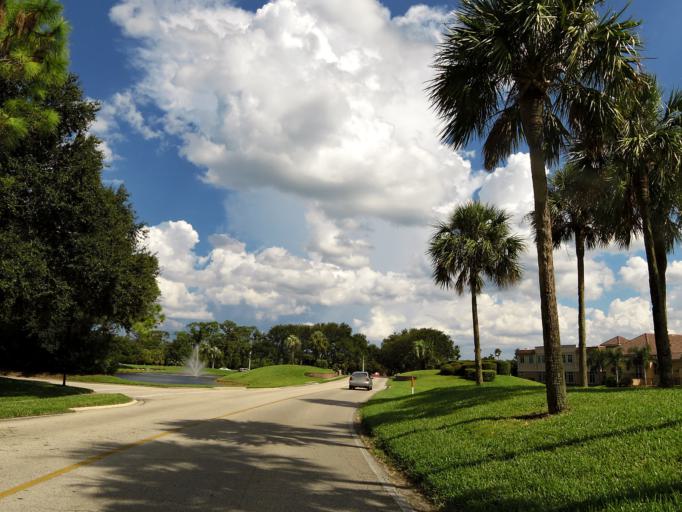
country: US
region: Florida
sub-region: Saint Johns County
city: Ponte Vedra Beach
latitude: 30.2490
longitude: -81.3895
